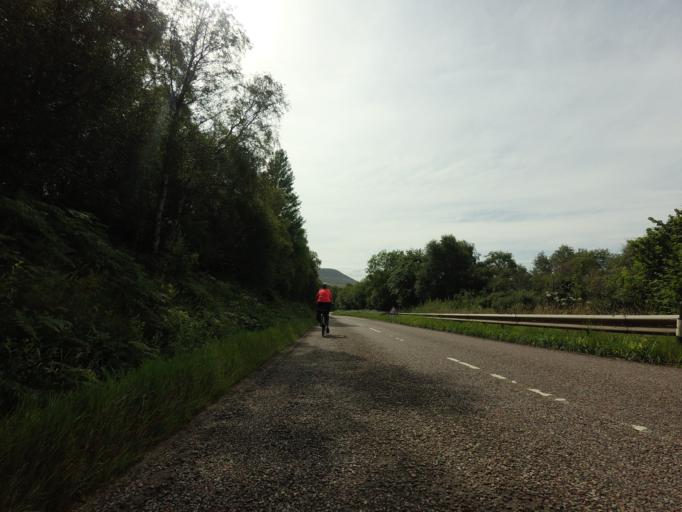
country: GB
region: Scotland
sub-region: Highland
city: Alness
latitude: 57.8523
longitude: -4.2614
